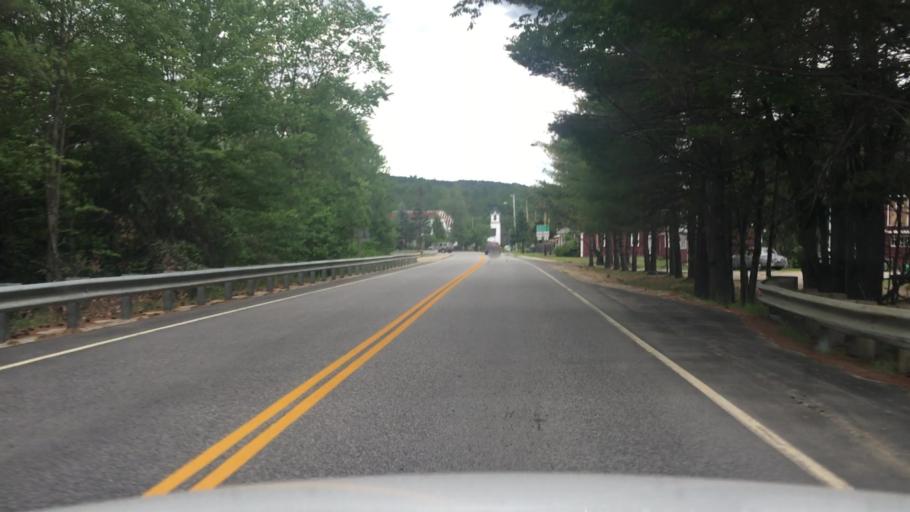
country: US
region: Maine
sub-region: Oxford County
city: Hartford
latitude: 44.3563
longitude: -70.3746
